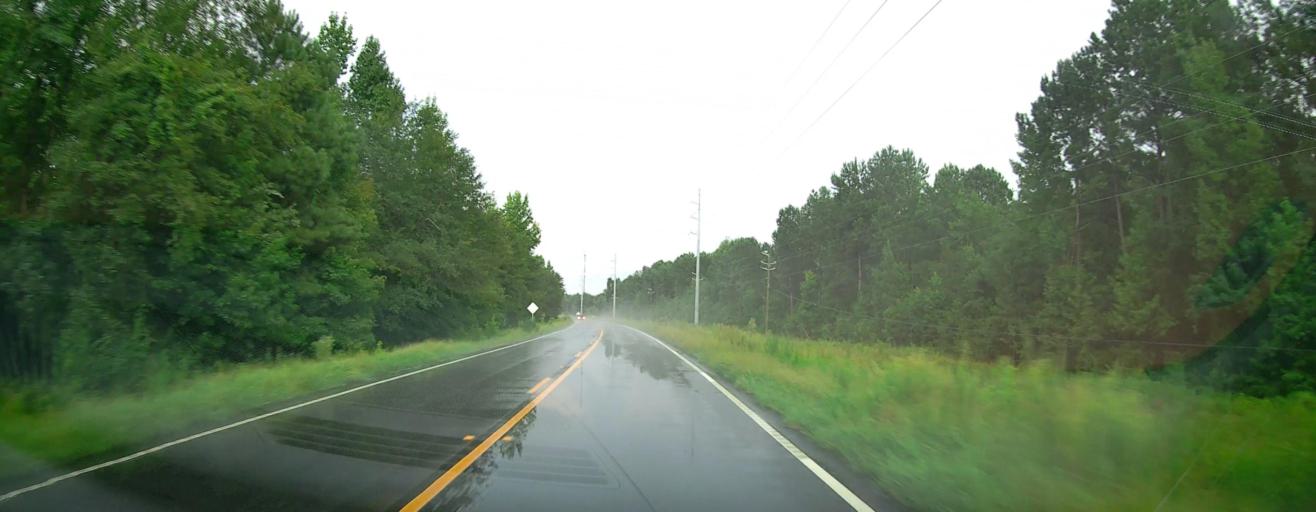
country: US
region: Georgia
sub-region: Twiggs County
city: Jeffersonville
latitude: 32.5745
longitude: -83.2006
